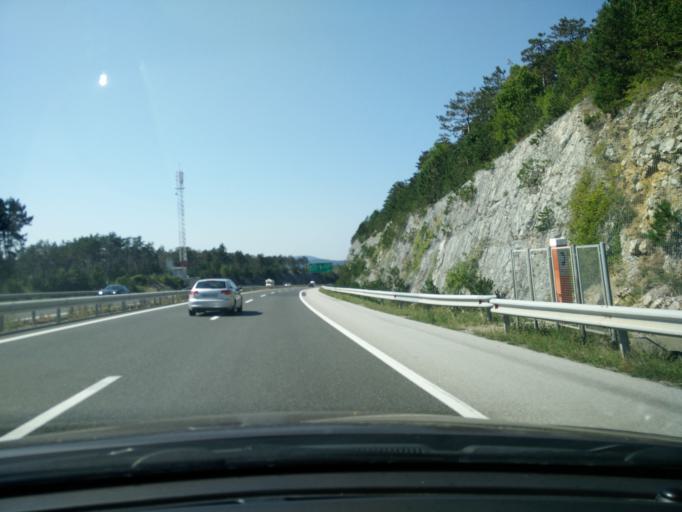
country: SI
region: Divaca
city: Divaca
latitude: 45.7034
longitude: 13.9975
